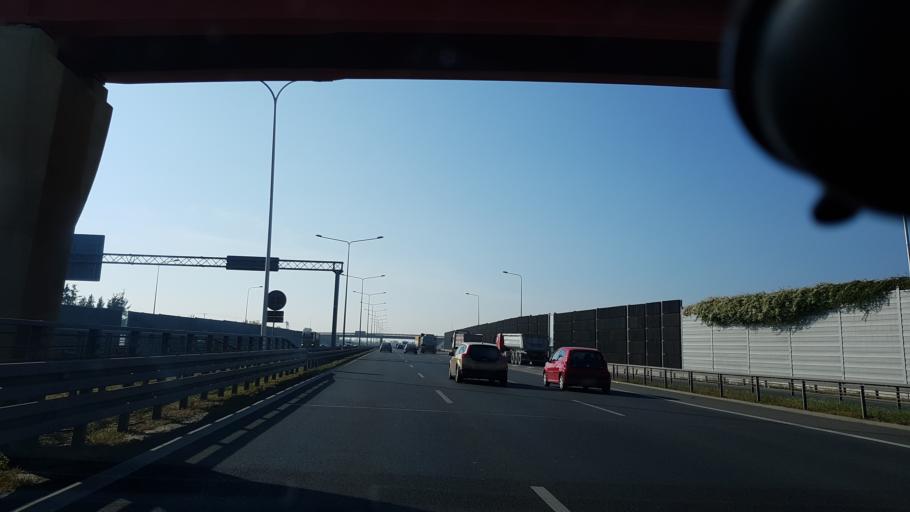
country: PL
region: Masovian Voivodeship
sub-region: Powiat pruszkowski
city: Nowe Grocholice
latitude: 52.1677
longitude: 20.9091
